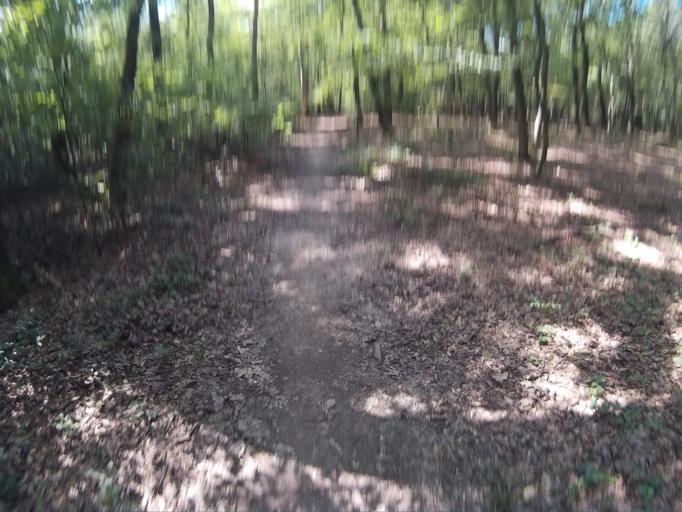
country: HU
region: Vas
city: Szombathely
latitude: 47.2196
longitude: 16.5588
